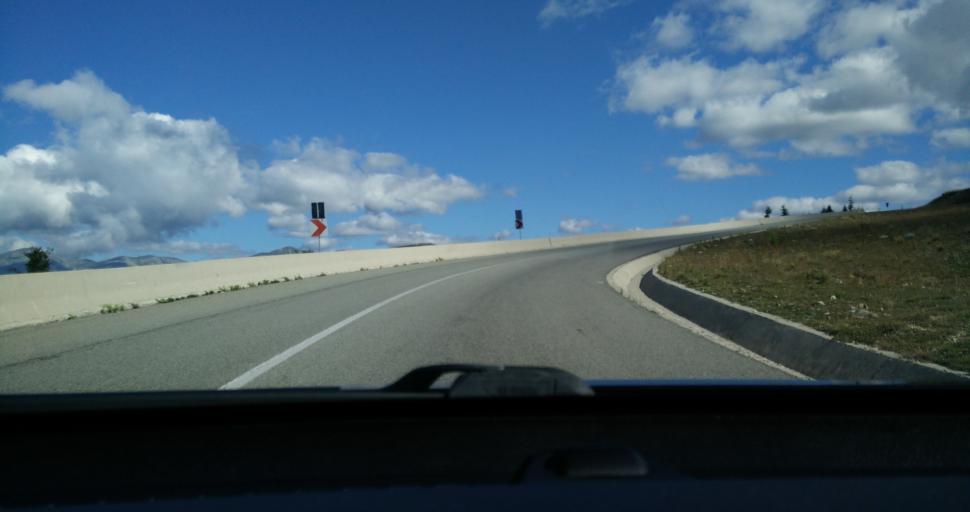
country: RO
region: Gorj
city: Novaci-Straini
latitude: 45.2492
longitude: 23.6941
